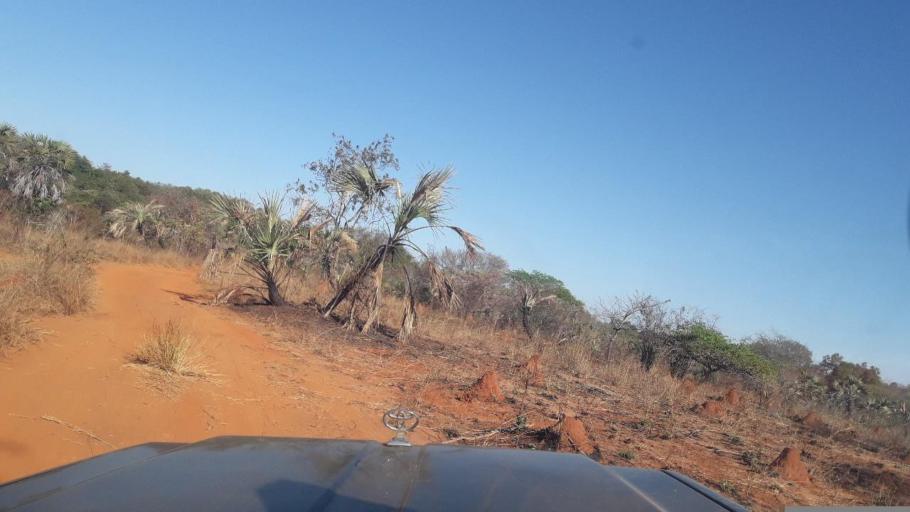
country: MG
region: Boeny
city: Sitampiky
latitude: -16.4070
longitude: 45.5994
